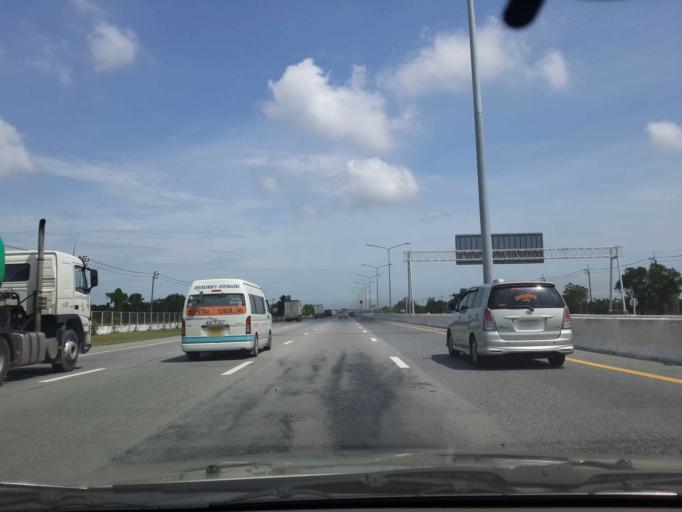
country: TH
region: Chachoengsao
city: Bang Pakong
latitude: 13.6110
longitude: 100.9355
